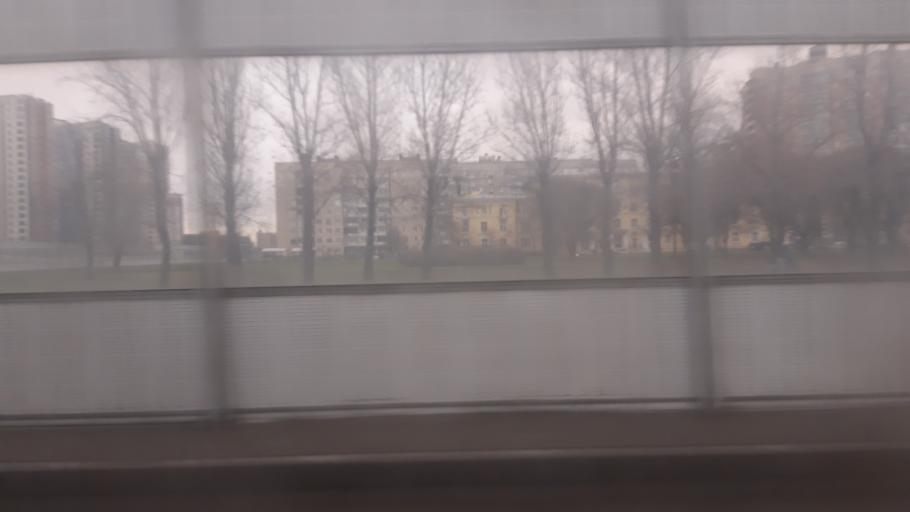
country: RU
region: St.-Petersburg
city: Kupchino
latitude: 59.8293
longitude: 30.3230
